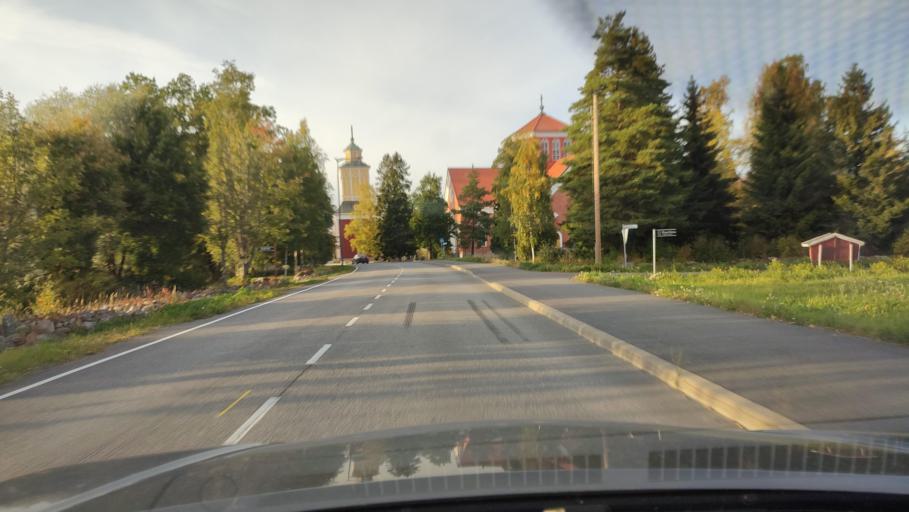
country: FI
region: Ostrobothnia
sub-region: Sydosterbotten
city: Kristinestad
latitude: 62.2453
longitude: 21.5210
